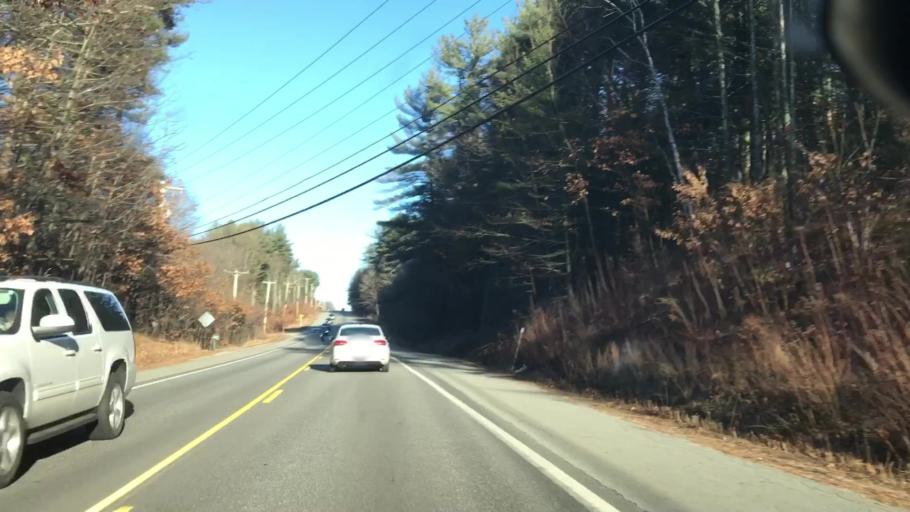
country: US
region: New Hampshire
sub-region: Hillsborough County
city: Bedford
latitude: 42.9138
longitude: -71.5515
